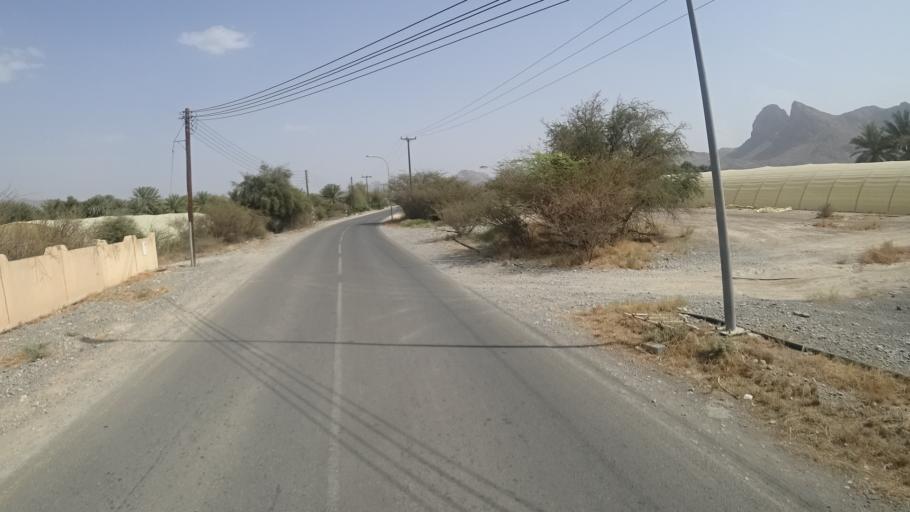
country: OM
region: Muhafazat ad Dakhiliyah
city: Bahla'
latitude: 23.1049
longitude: 57.2991
